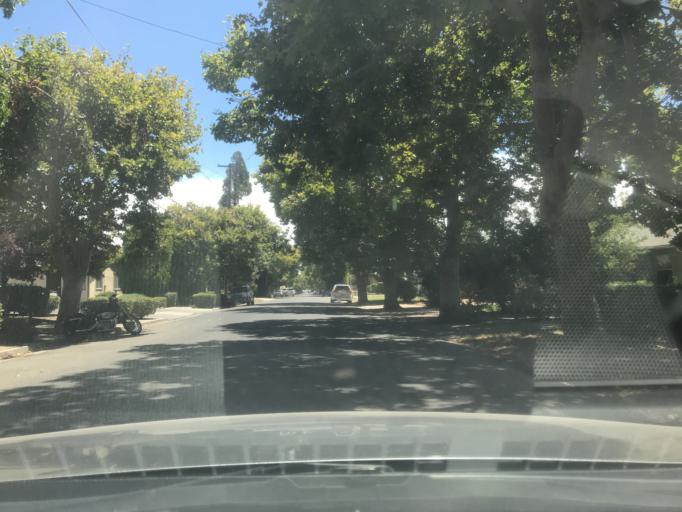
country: US
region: California
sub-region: Merced County
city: Atwater
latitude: 37.3510
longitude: -120.6129
